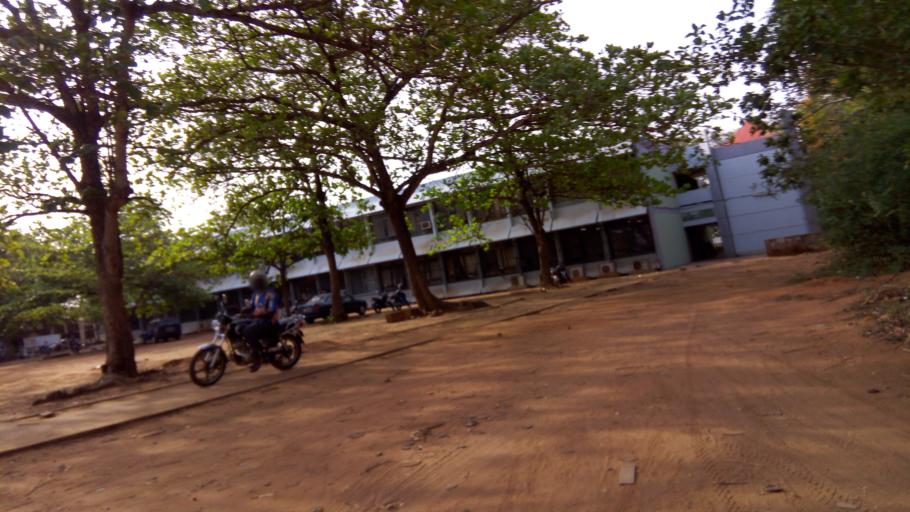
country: TG
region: Maritime
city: Lome
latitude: 6.1753
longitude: 1.2132
